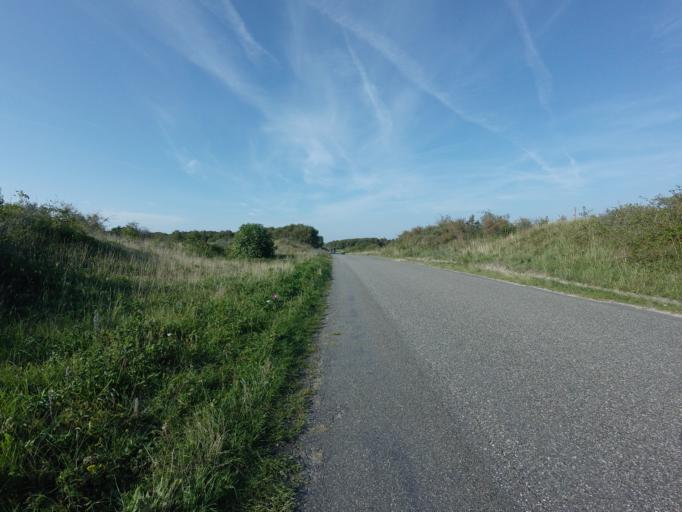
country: NL
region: Friesland
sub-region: Gemeente Schiermonnikoog
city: Schiermonnikoog
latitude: 53.4915
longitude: 6.1841
